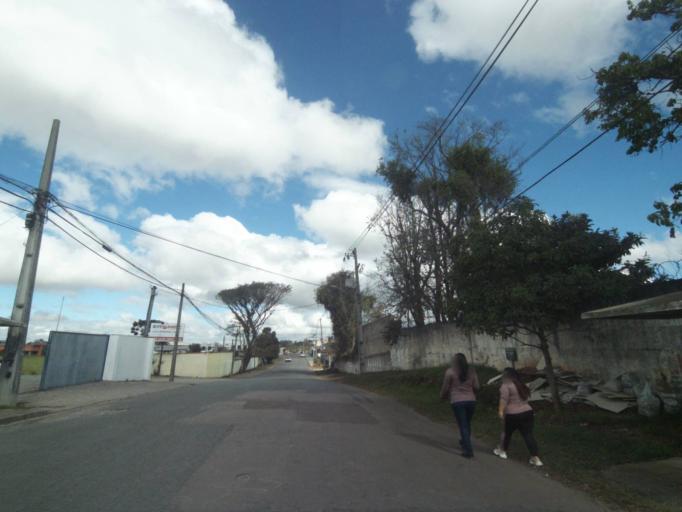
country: BR
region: Parana
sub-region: Sao Jose Dos Pinhais
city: Sao Jose dos Pinhais
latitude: -25.5349
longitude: -49.2943
